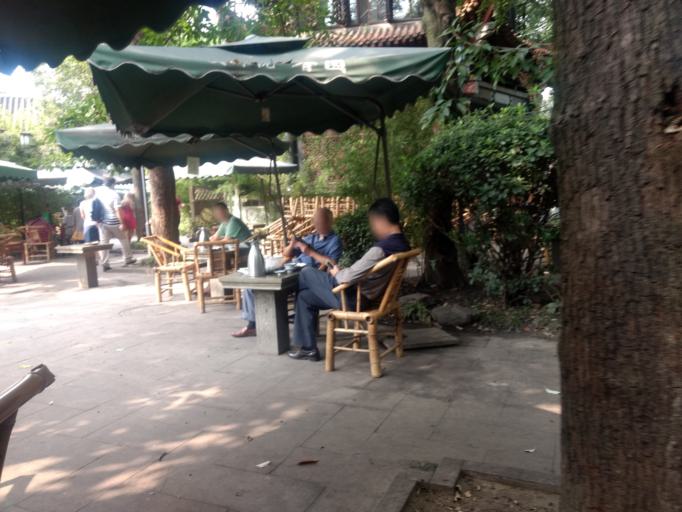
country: CN
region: Sichuan
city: Chengdu
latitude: 30.6769
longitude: 104.0707
